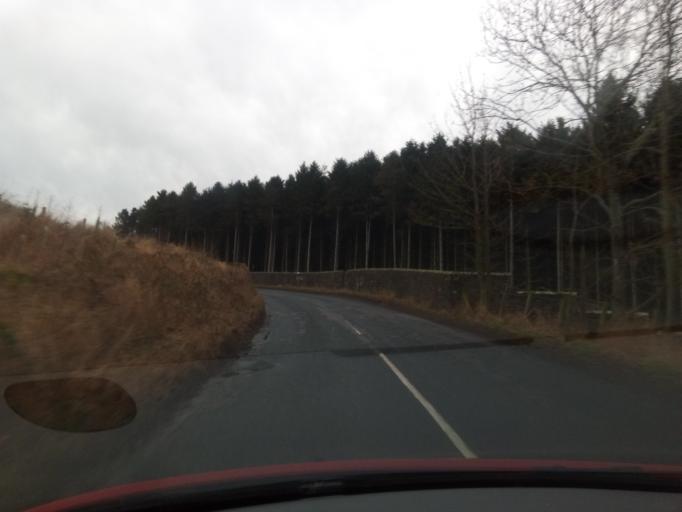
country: GB
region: England
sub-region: Northumberland
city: Alnwick
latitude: 55.4502
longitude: -1.7577
